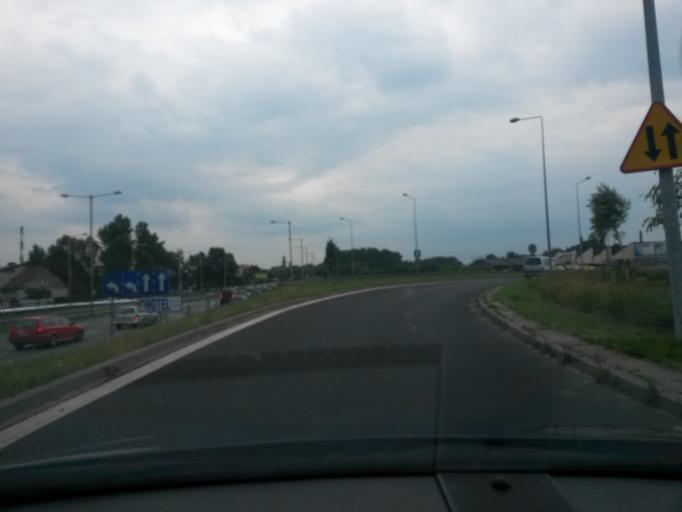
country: PL
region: Silesian Voivodeship
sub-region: Czestochowa
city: Czestochowa
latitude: 50.8072
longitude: 19.1353
